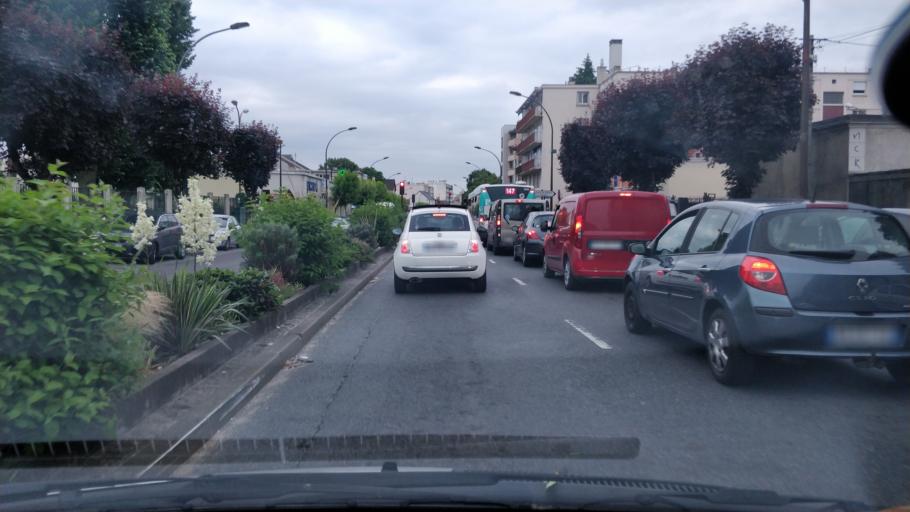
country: FR
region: Ile-de-France
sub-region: Departement de Seine-Saint-Denis
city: Livry-Gargan
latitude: 48.9204
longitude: 2.5399
